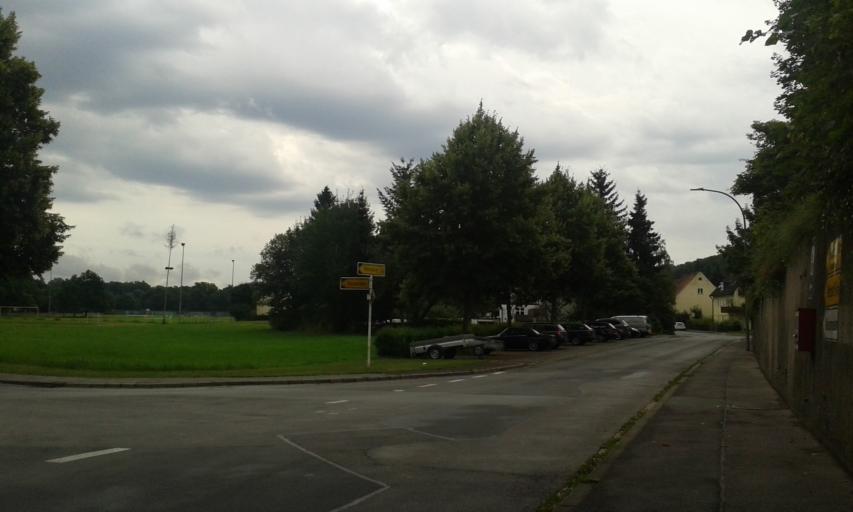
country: DE
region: Bavaria
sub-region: Upper Franconia
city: Bamberg
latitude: 49.8672
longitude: 10.9076
